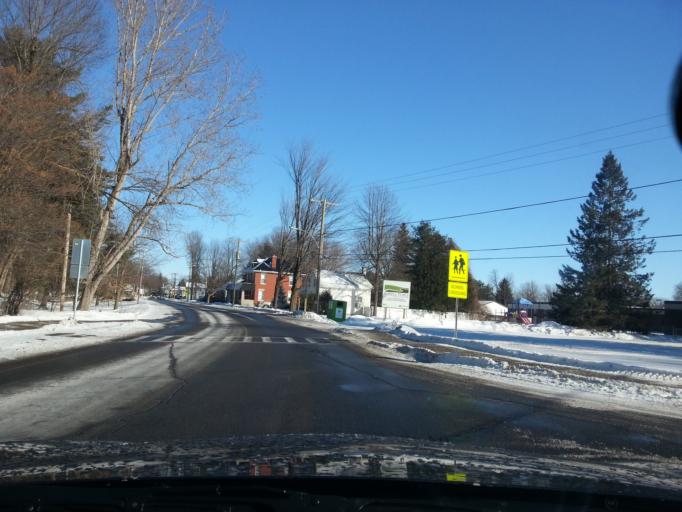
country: CA
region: Ontario
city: Bourget
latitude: 45.2576
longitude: -75.3641
